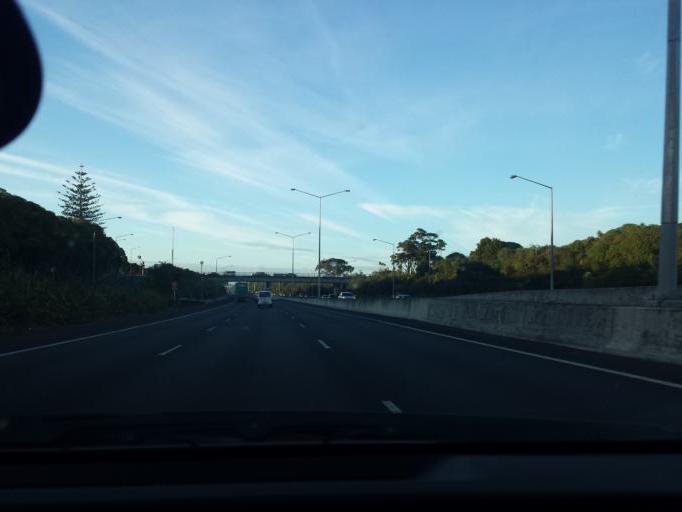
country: NZ
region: Auckland
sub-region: Auckland
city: Mangere
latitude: -36.9518
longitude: 174.7947
